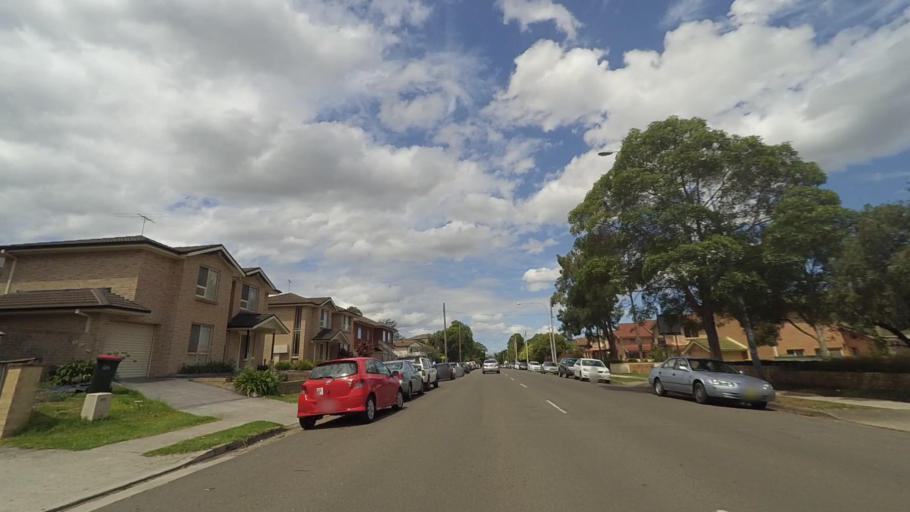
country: AU
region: New South Wales
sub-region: Fairfield
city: Fairfield Heights
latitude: -33.8693
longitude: 150.9494
